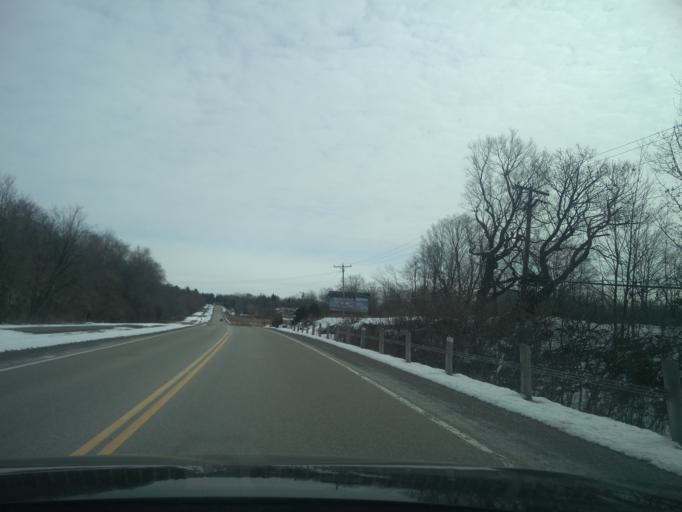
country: US
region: New York
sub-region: Jefferson County
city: Clayton
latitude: 44.3503
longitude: -76.0472
